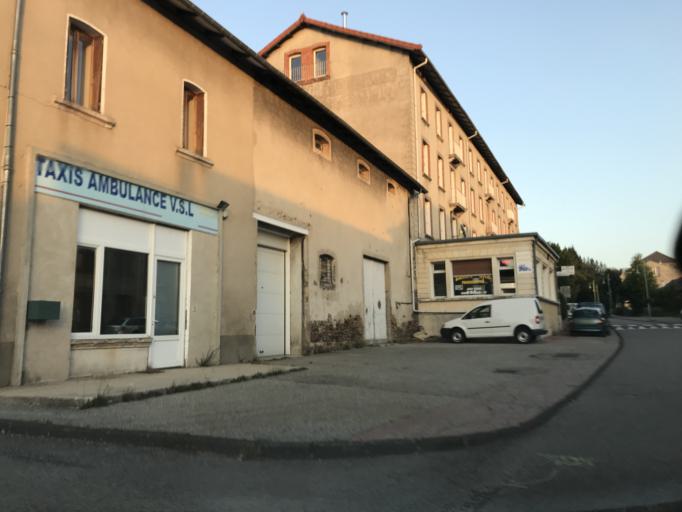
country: FR
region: Rhone-Alpes
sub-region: Departement de l'Ardeche
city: Saint-Agreve
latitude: 45.0141
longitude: 4.3885
